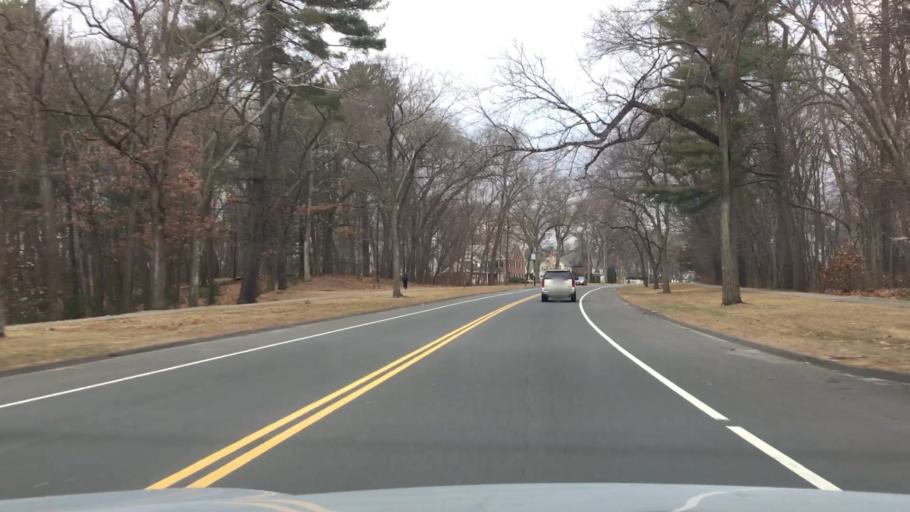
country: US
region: Massachusetts
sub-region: Hampden County
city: Longmeadow
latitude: 42.0603
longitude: -72.5729
